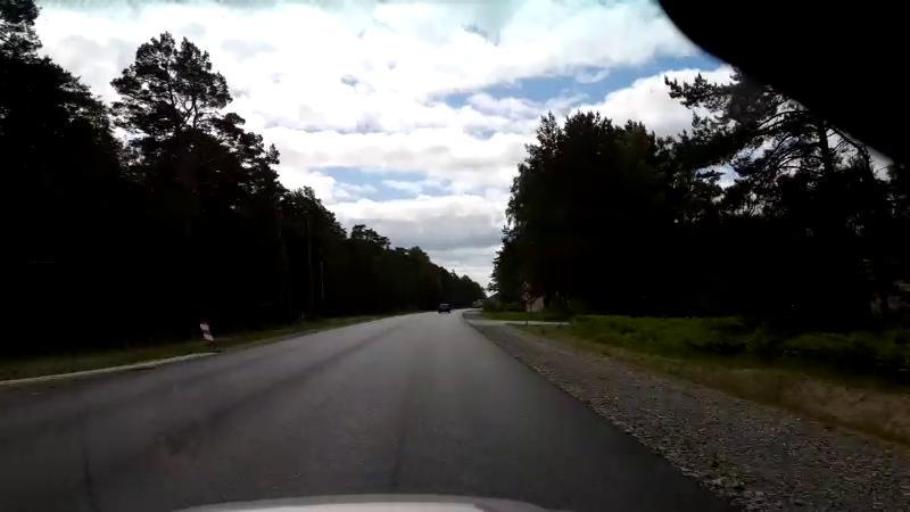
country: LV
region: Salacgrivas
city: Ainazi
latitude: 57.8169
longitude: 24.3471
